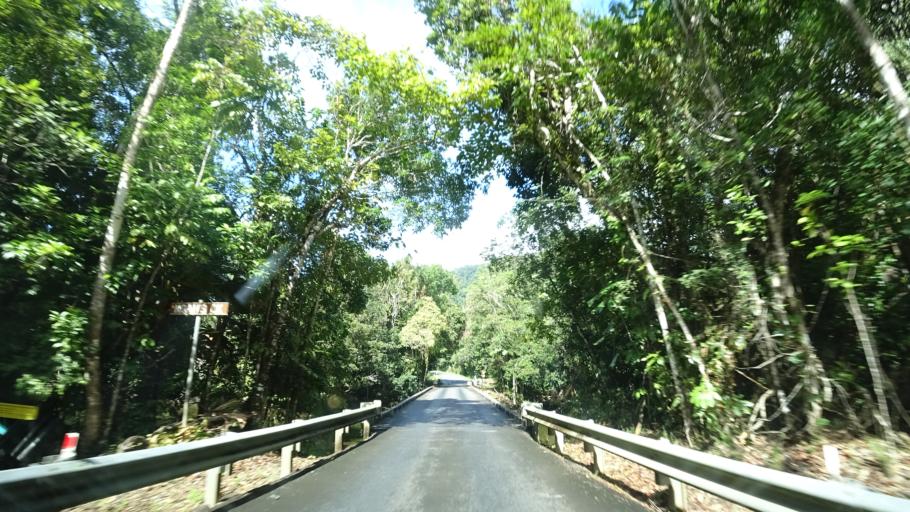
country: AU
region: Queensland
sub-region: Cairns
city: Port Douglas
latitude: -16.1398
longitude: 145.4307
